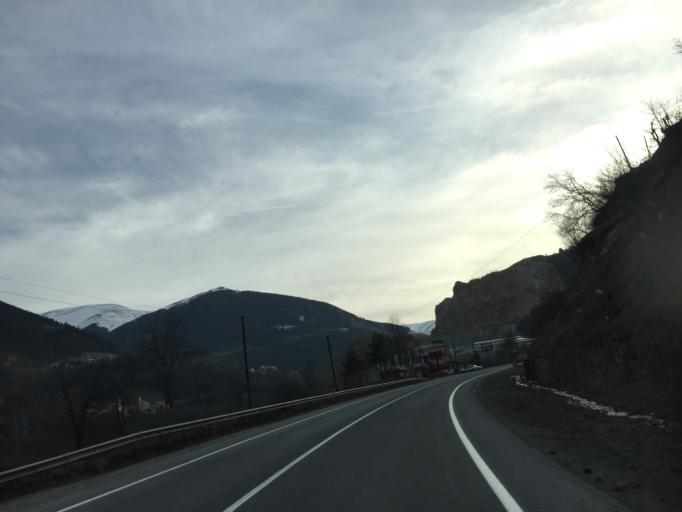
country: TR
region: Trabzon
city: Macka
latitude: 40.7197
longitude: 39.5174
